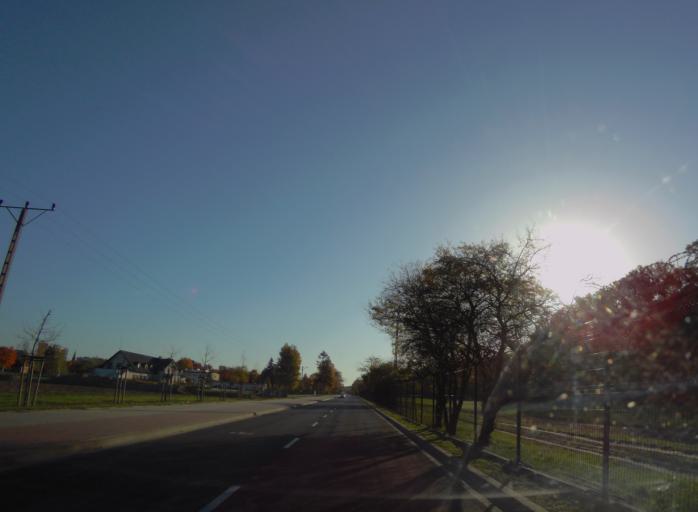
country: PL
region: Masovian Voivodeship
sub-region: Powiat pruszkowski
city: Granica
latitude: 52.1529
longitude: 20.7799
